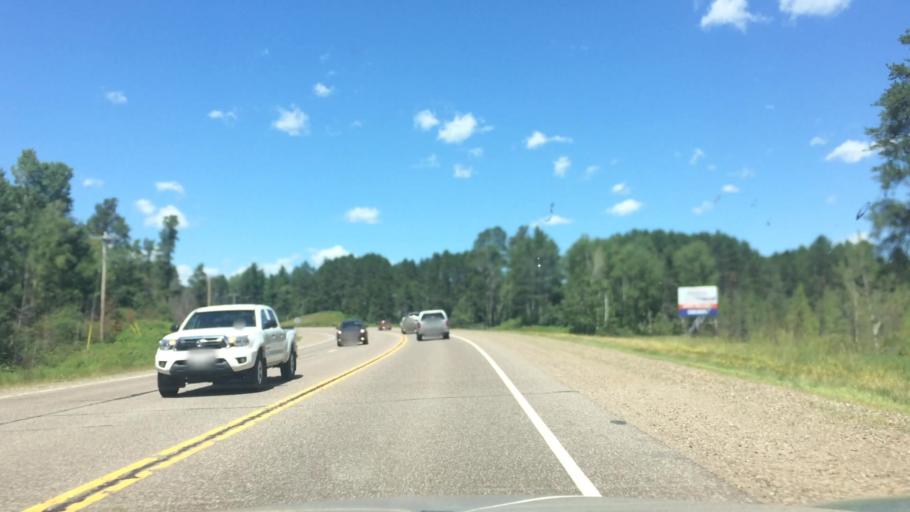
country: US
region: Wisconsin
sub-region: Lincoln County
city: Tomahawk
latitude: 45.6547
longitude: -89.7049
